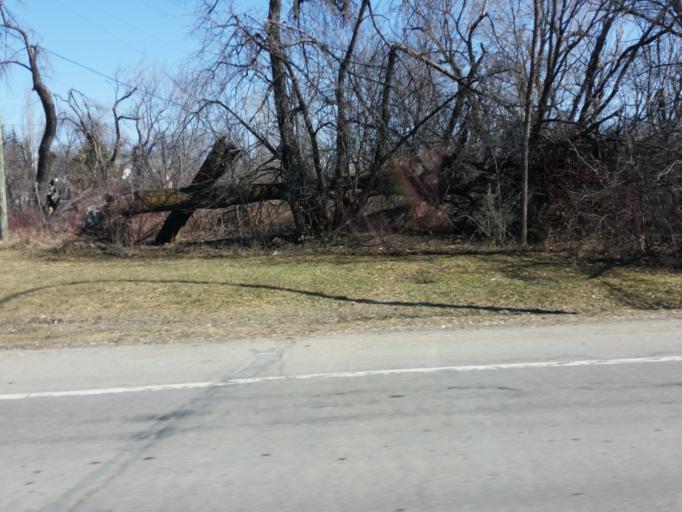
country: US
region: North Dakota
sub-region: Walsh County
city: Grafton
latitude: 48.2860
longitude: -97.3713
